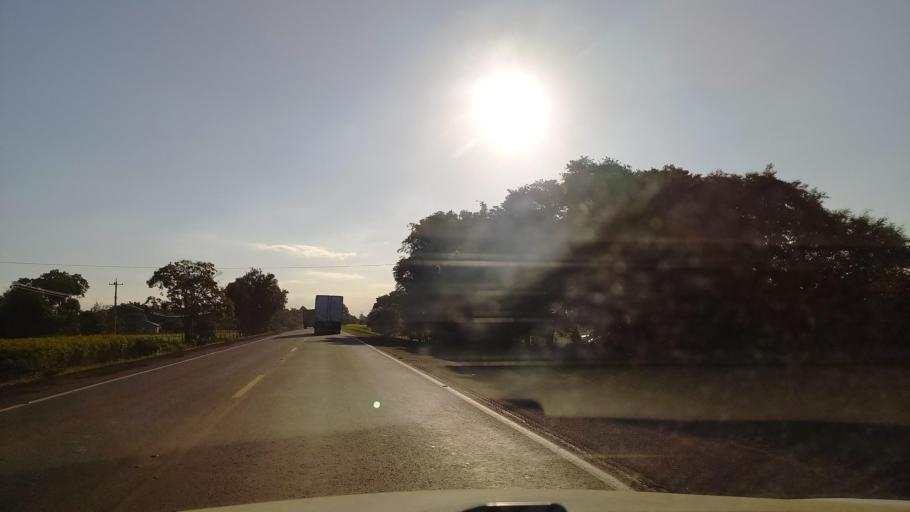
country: BR
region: Rio Grande do Sul
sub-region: Venancio Aires
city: Venancio Aires
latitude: -29.6627
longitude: -52.0631
